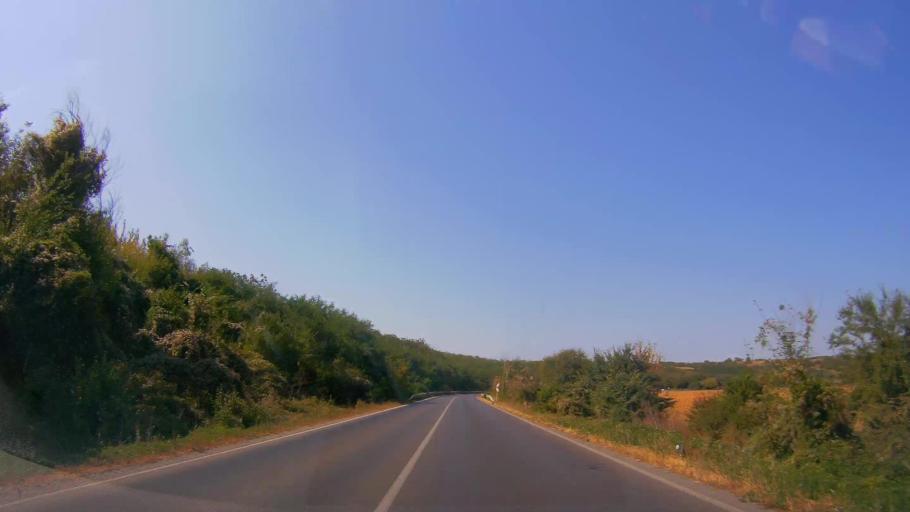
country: BG
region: Razgrad
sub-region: Obshtina Tsar Kaloyan
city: Tsar Kaloyan
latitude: 43.6147
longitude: 26.2173
